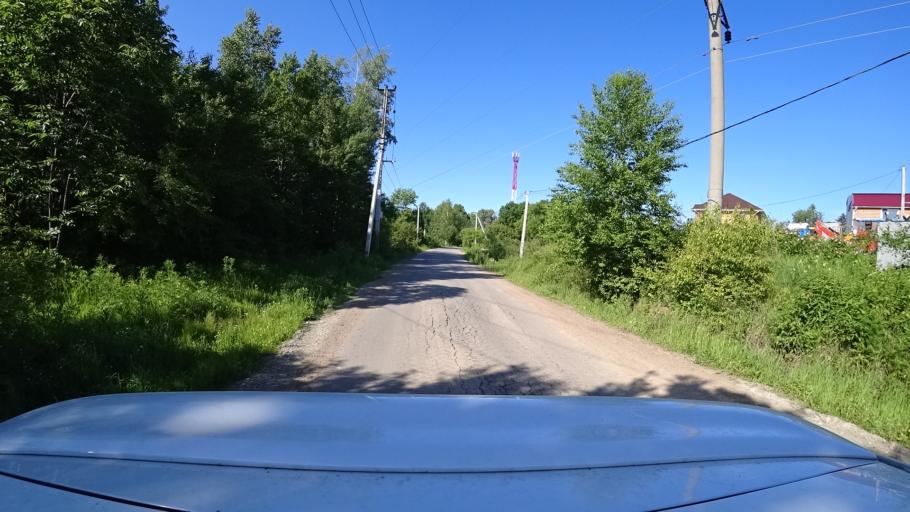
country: RU
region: Khabarovsk Krai
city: Topolevo
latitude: 48.5466
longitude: 135.1849
